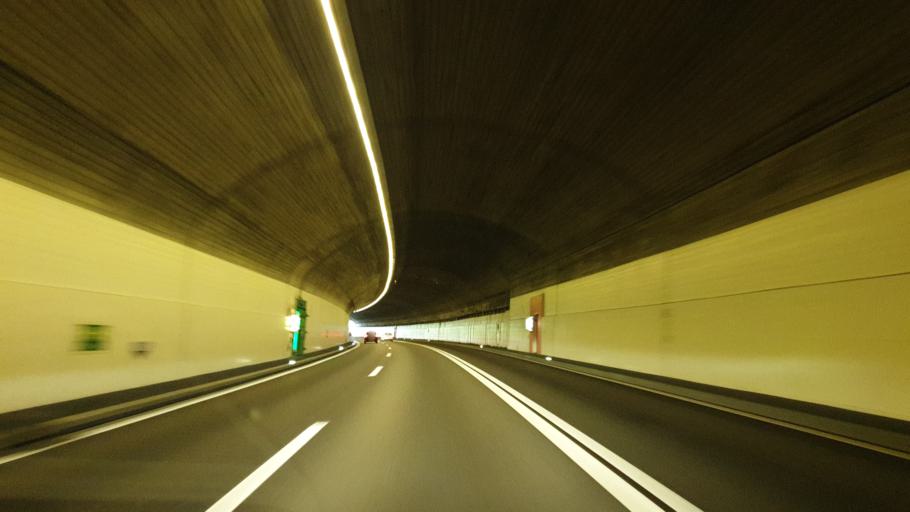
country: CH
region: Zurich
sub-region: Bezirk Dietikon
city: Urdorf / Bodenfeld
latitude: 47.3885
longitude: 8.4141
